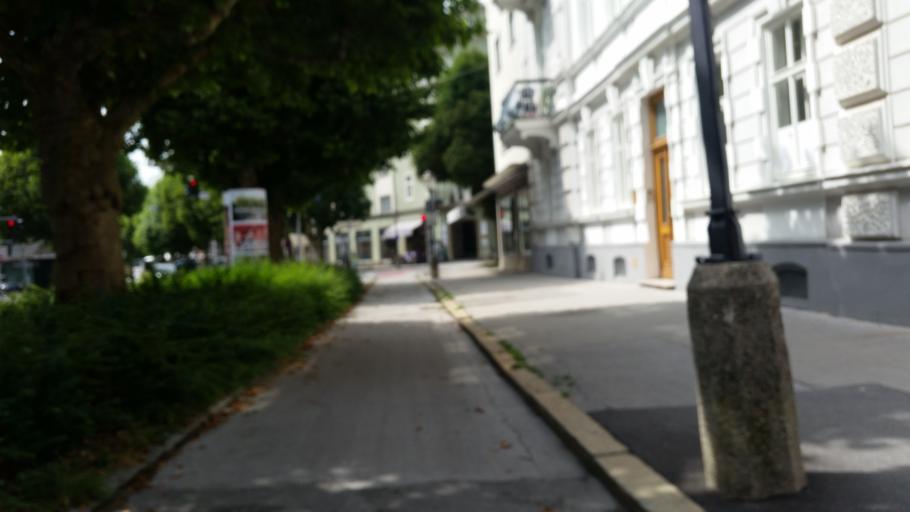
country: AT
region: Salzburg
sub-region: Salzburg Stadt
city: Salzburg
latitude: 47.8071
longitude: 13.0471
